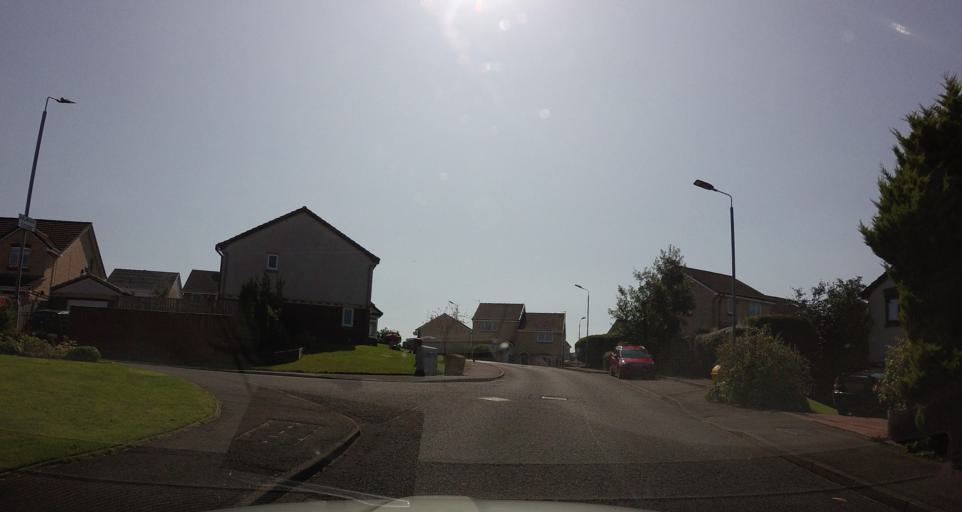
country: GB
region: Scotland
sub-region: South Lanarkshire
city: East Kilbride
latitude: 55.7399
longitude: -4.1998
